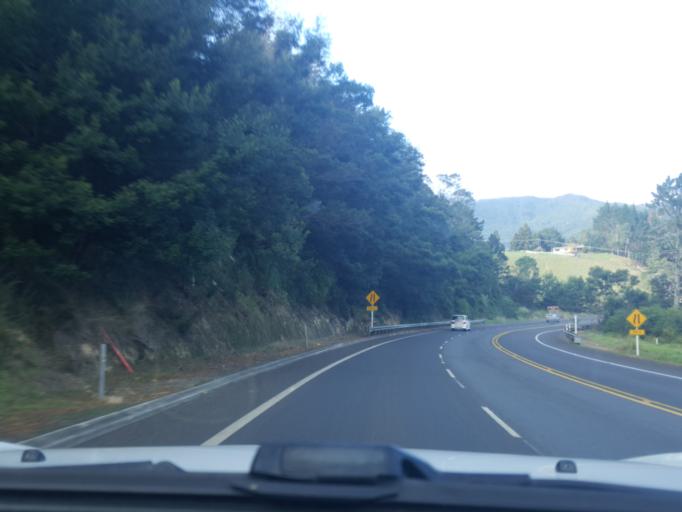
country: NZ
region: Waikato
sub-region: Hauraki District
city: Paeroa
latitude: -37.4032
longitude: 175.7076
